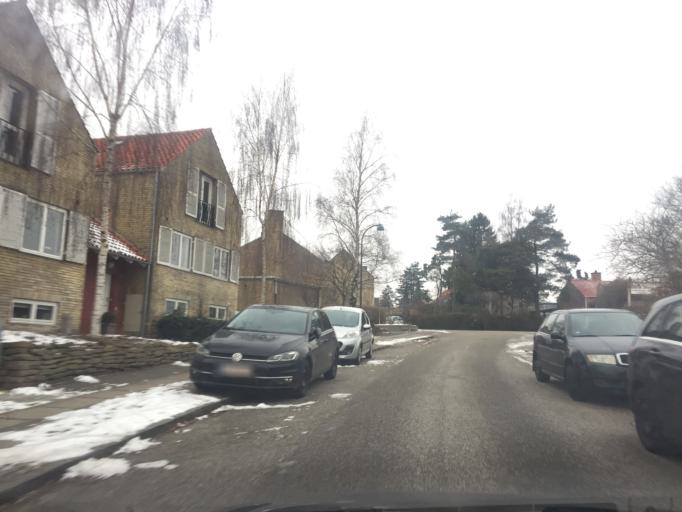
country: DK
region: Capital Region
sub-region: Lyngby-Tarbaek Kommune
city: Kongens Lyngby
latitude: 55.7597
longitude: 12.5311
